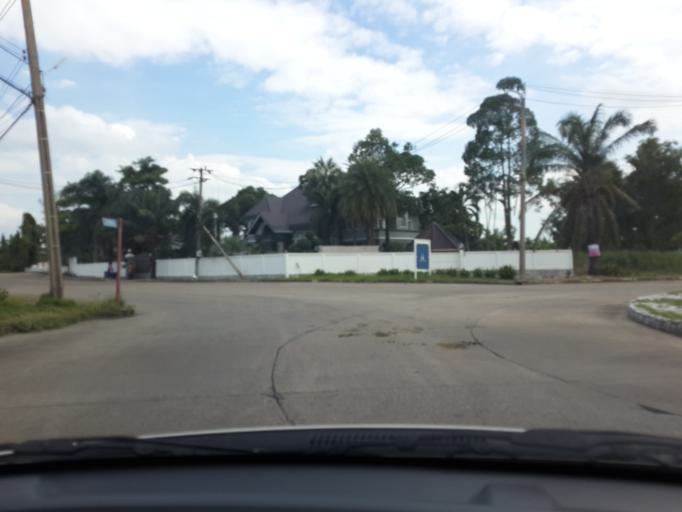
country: TH
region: Bangkok
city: Khlong Sam Wa
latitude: 13.8407
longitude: 100.7635
